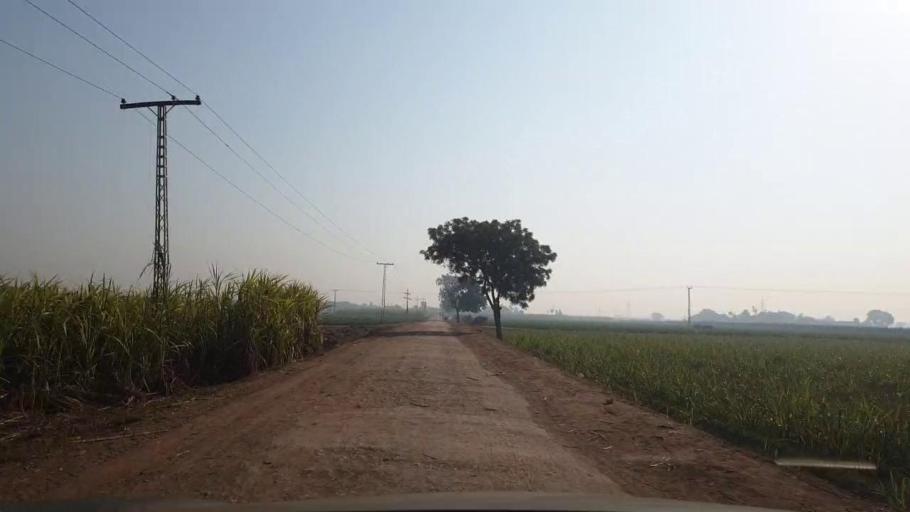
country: PK
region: Sindh
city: Tando Allahyar
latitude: 25.4919
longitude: 68.7252
